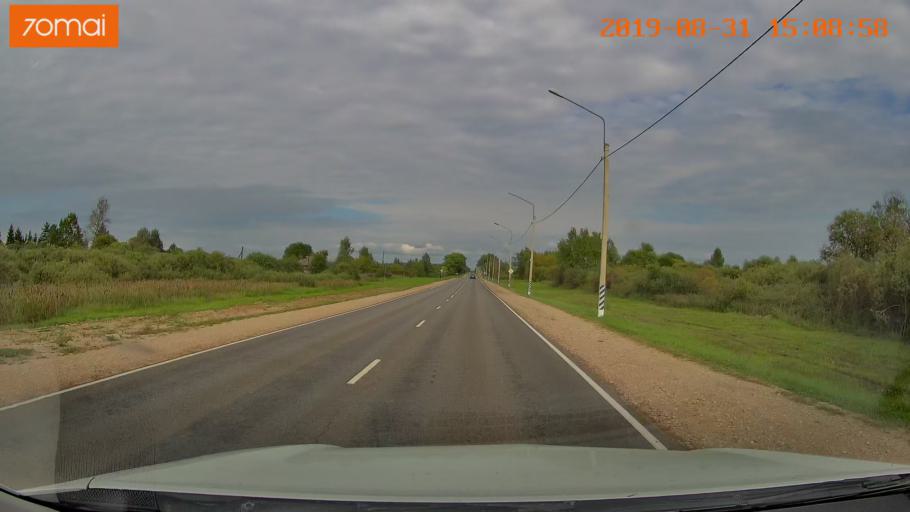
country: RU
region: Kaluga
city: Spas-Demensk
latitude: 54.3968
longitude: 34.1923
